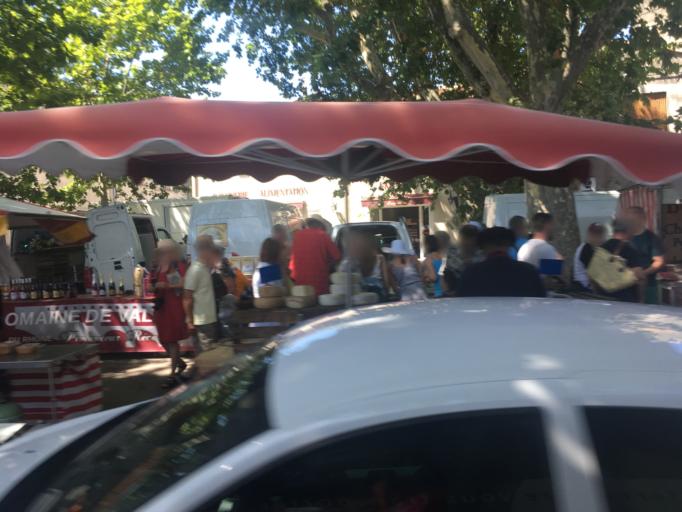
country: FR
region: Provence-Alpes-Cote d'Azur
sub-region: Departement des Bouches-du-Rhone
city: Arles
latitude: 43.6809
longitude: 4.6333
